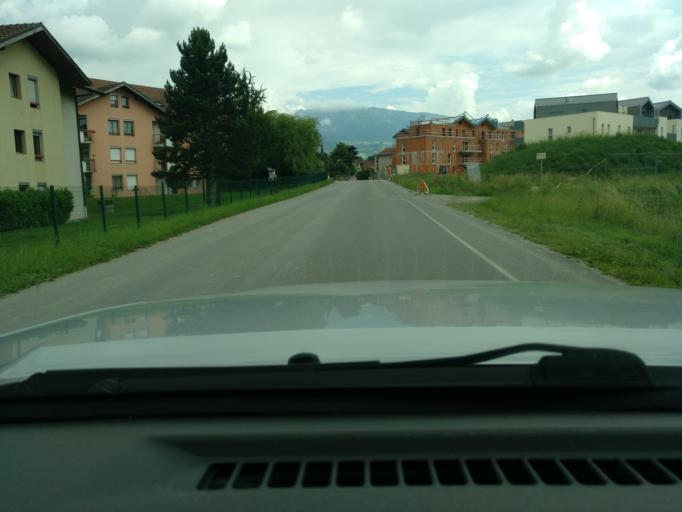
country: FR
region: Rhone-Alpes
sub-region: Departement de la Haute-Savoie
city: Cornier
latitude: 46.0955
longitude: 6.2994
